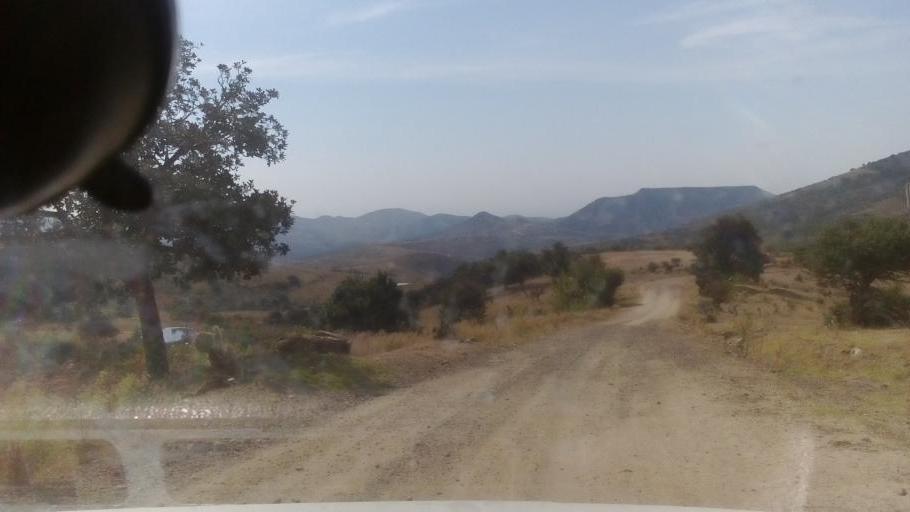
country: MX
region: Guanajuato
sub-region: Leon
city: Lucio Blanco (Los Gavilanes)
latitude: 21.2033
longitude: -101.4984
